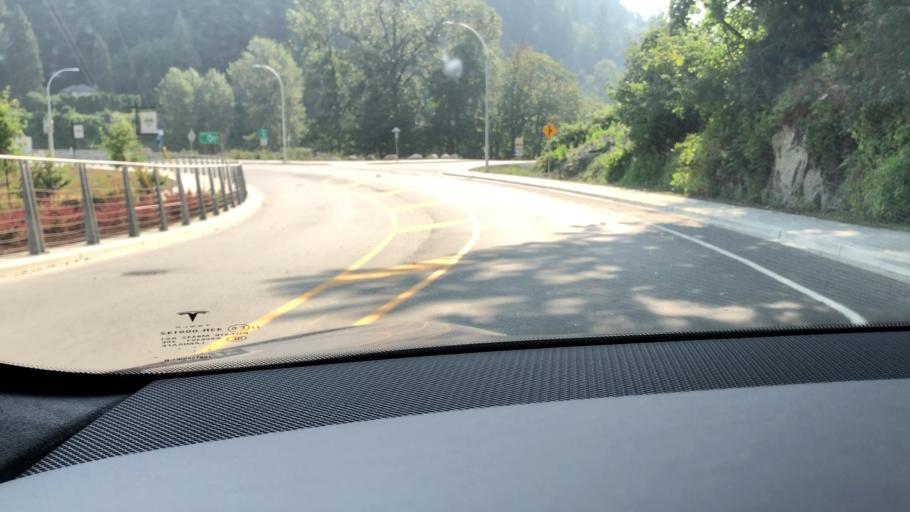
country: CA
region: British Columbia
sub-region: Fraser Valley Regional District
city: Chilliwack
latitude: 49.0971
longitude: -121.9649
